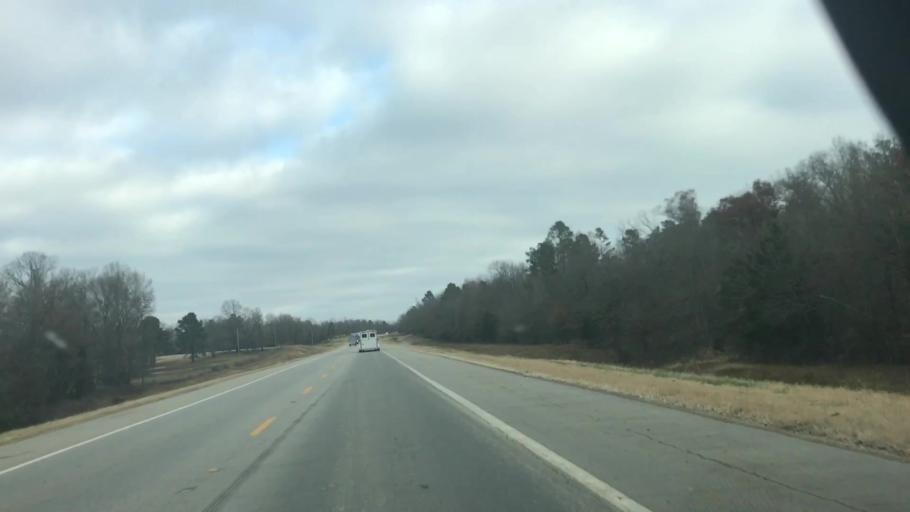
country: US
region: Arkansas
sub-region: Scott County
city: Waldron
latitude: 34.9153
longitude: -94.1071
